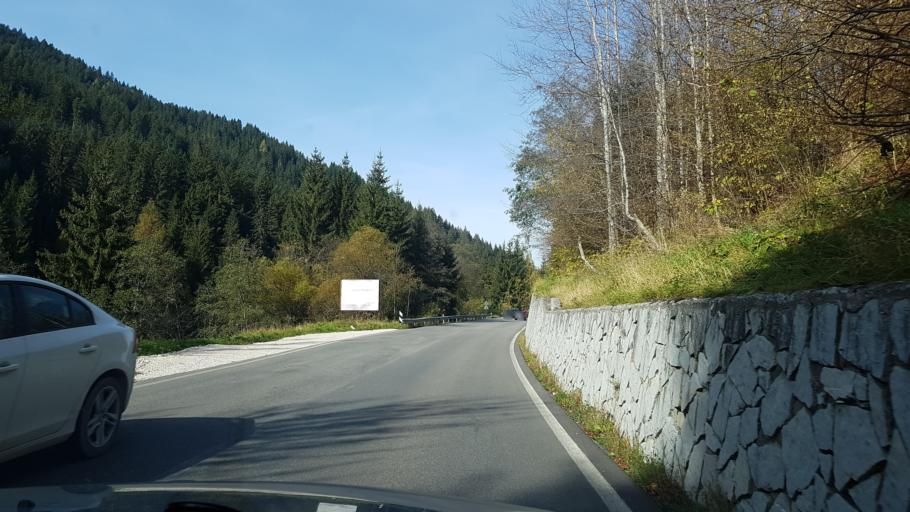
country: IT
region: Veneto
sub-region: Provincia di Belluno
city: Santo Stefano di Cadore
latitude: 46.5679
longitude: 12.5392
